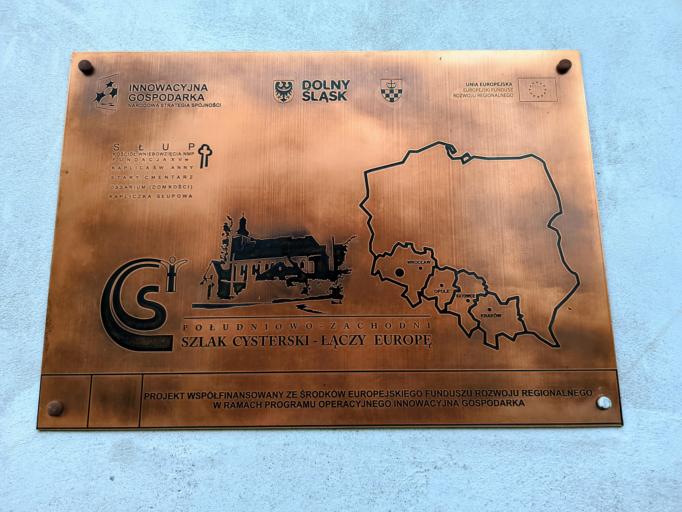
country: PL
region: Lower Silesian Voivodeship
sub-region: Powiat jaworski
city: Paszowice
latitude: 51.0969
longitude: 16.1009
